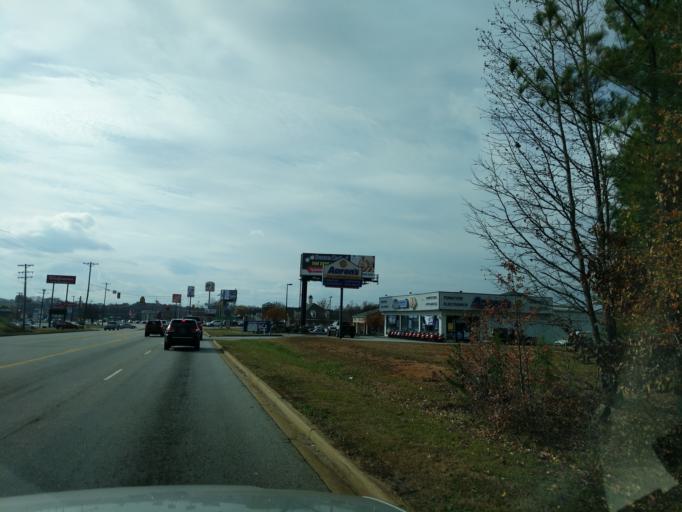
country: US
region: South Carolina
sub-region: Oconee County
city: Seneca
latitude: 34.6912
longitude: -82.9909
